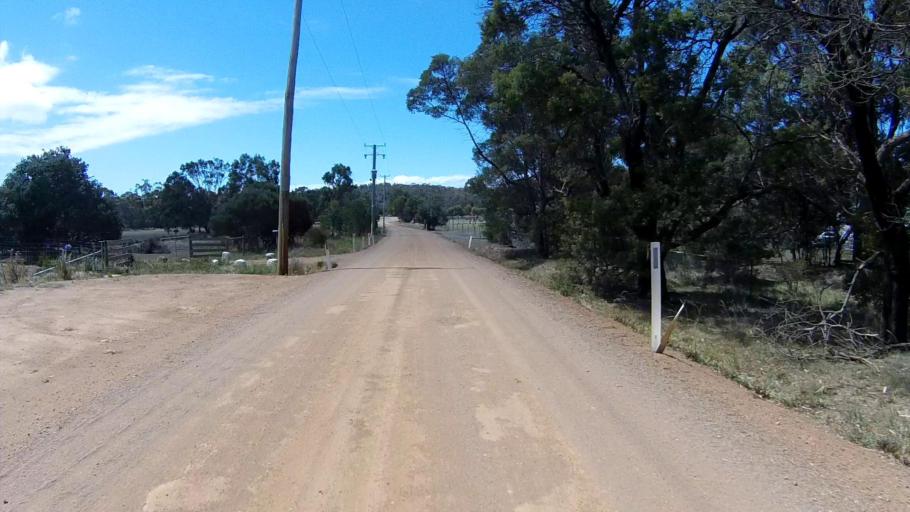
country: AU
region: Tasmania
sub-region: Clarence
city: Sandford
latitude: -42.9655
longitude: 147.4711
